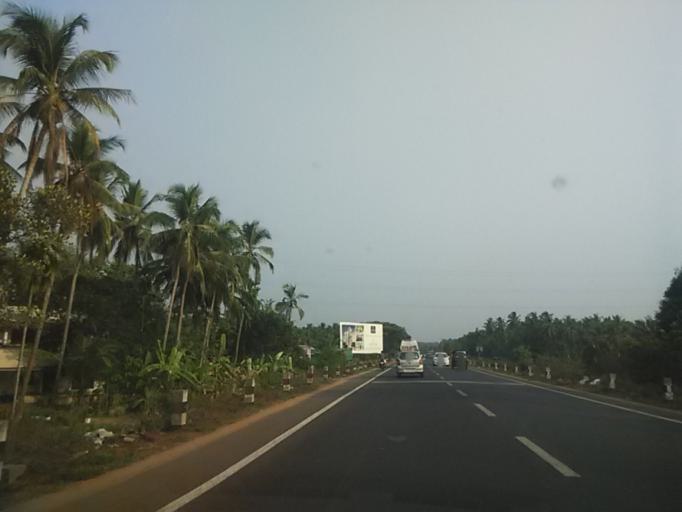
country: IN
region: Kerala
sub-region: Kozhikode
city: Kozhikode
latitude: 11.3176
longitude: 75.7780
